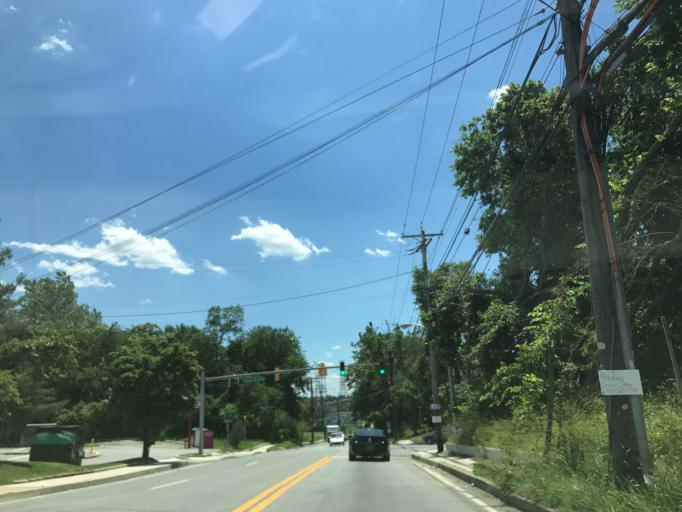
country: US
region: Maryland
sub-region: Anne Arundel County
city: Glen Burnie
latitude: 39.1863
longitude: -76.6139
